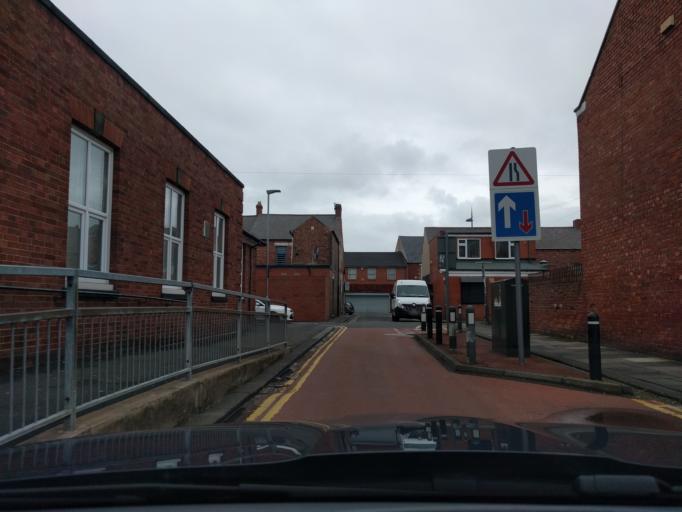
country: GB
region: England
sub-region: Northumberland
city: Ashington
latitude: 55.1824
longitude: -1.5696
